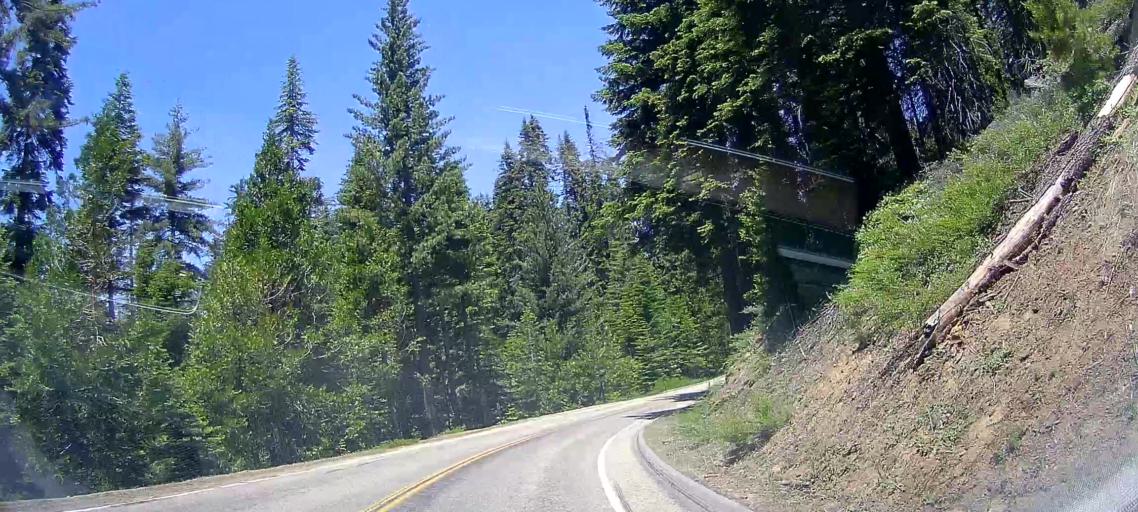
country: US
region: California
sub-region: Tulare County
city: Three Rivers
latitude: 36.7187
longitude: -118.9556
